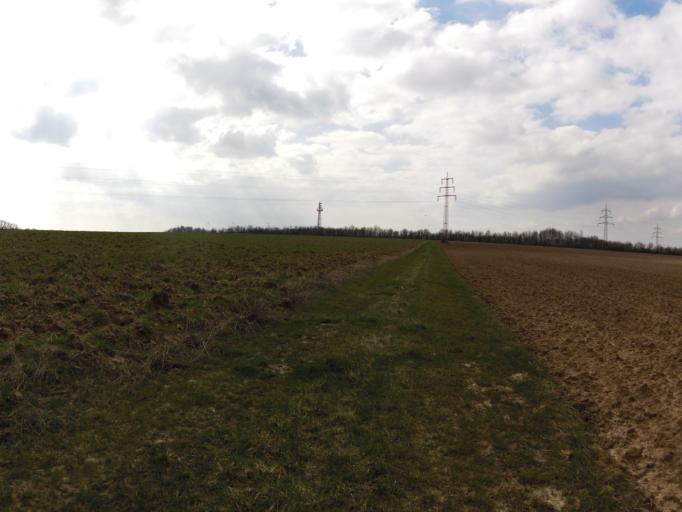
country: DE
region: Bavaria
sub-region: Regierungsbezirk Unterfranken
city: Buchbrunn
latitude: 49.7404
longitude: 10.1117
